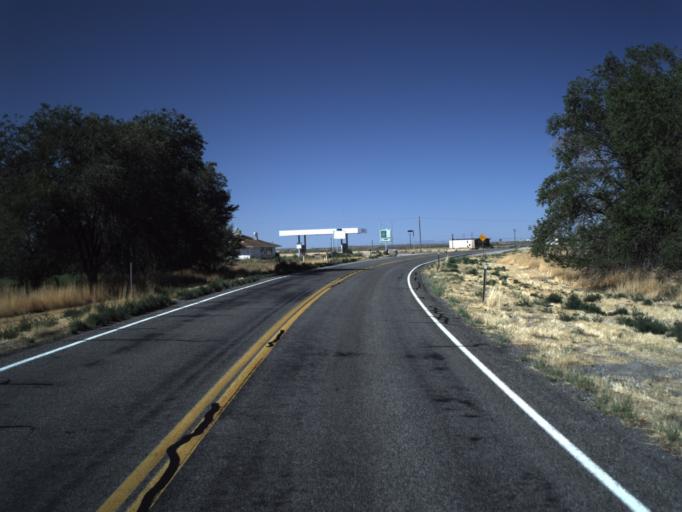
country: US
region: Utah
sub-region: Millard County
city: Delta
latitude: 39.5146
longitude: -112.3732
